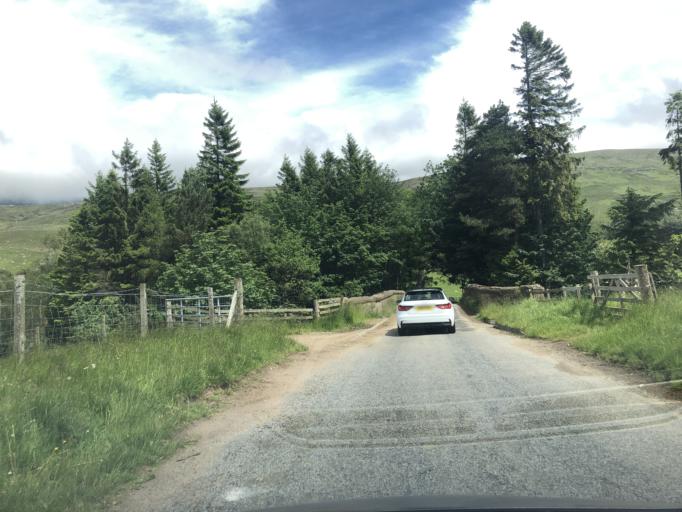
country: GB
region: Scotland
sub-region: Angus
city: Kirriemuir
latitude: 56.8415
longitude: -3.1072
